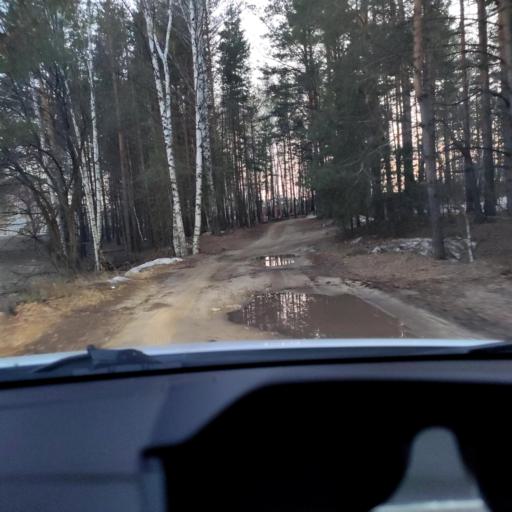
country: RU
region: Tatarstan
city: Stolbishchi
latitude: 55.6434
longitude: 49.1076
